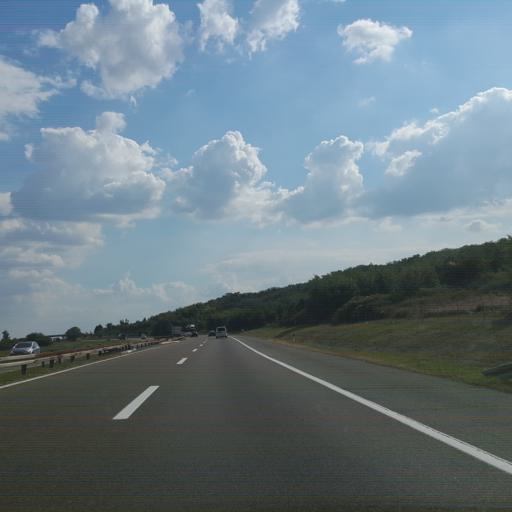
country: RS
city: Lugavcina
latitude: 44.4506
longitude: 21.0453
